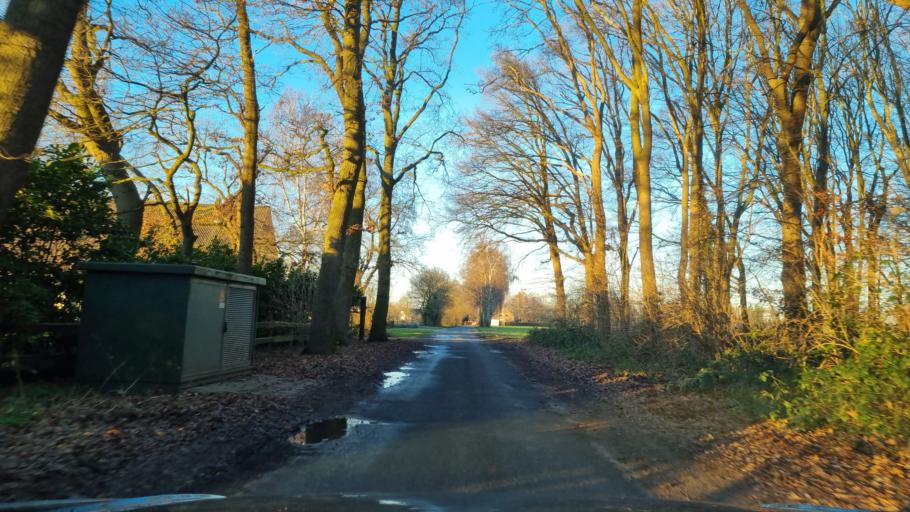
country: DE
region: North Rhine-Westphalia
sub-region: Regierungsbezirk Dusseldorf
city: Kranenburg
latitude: 51.7746
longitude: 6.0553
